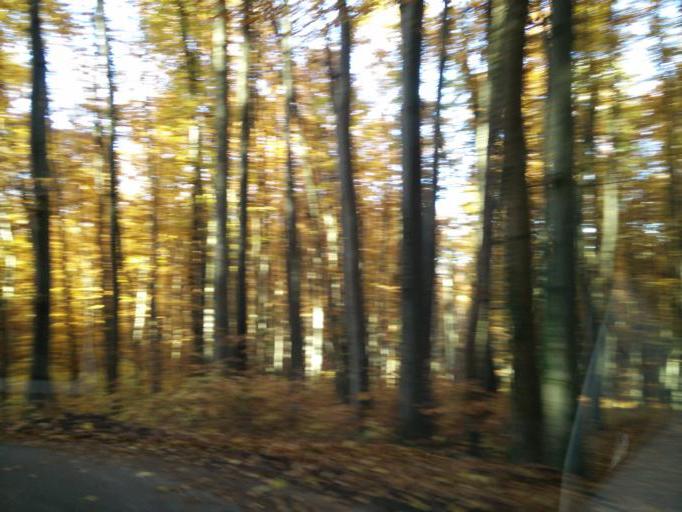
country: DE
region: Baden-Wuerttemberg
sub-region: Tuebingen Region
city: Gomaringen
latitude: 48.4246
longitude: 9.1104
